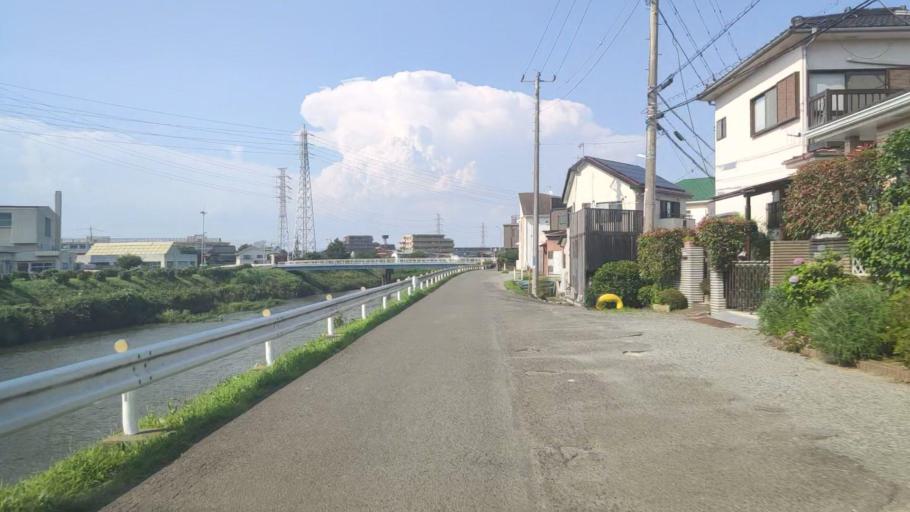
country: JP
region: Kanagawa
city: Hiratsuka
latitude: 35.3470
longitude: 139.3254
